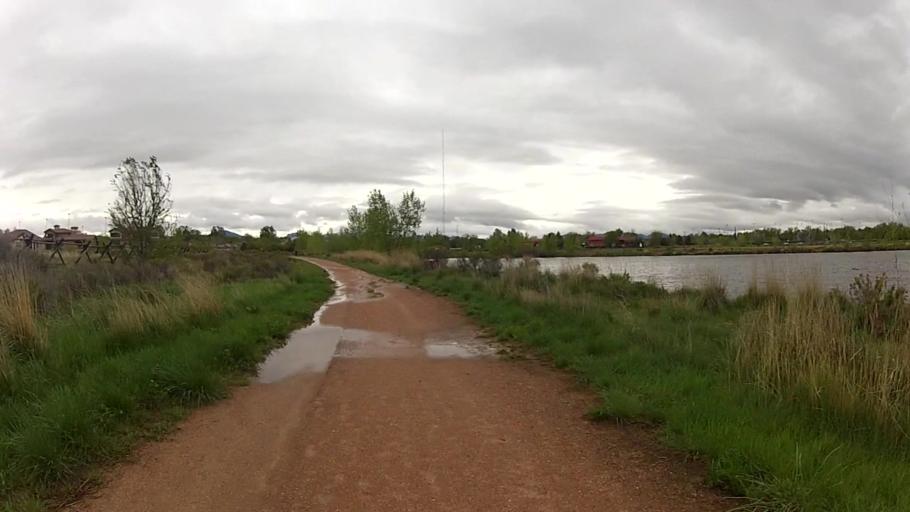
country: US
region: Colorado
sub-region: Larimer County
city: Loveland
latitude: 40.3894
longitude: -105.0943
